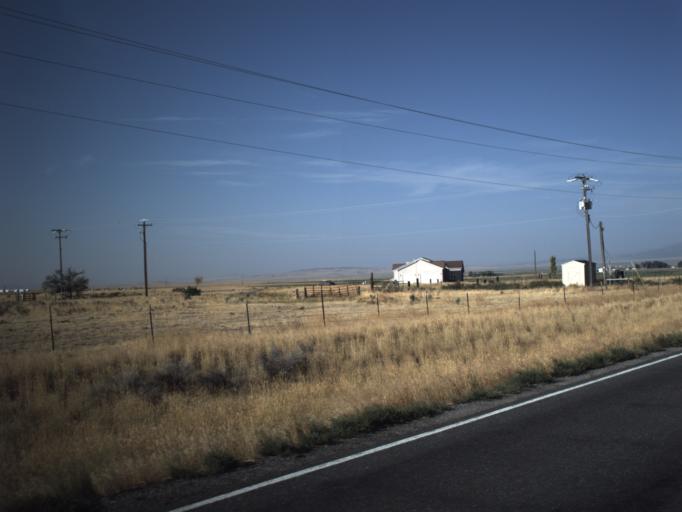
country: US
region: Idaho
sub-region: Oneida County
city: Malad City
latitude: 41.9675
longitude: -112.8132
